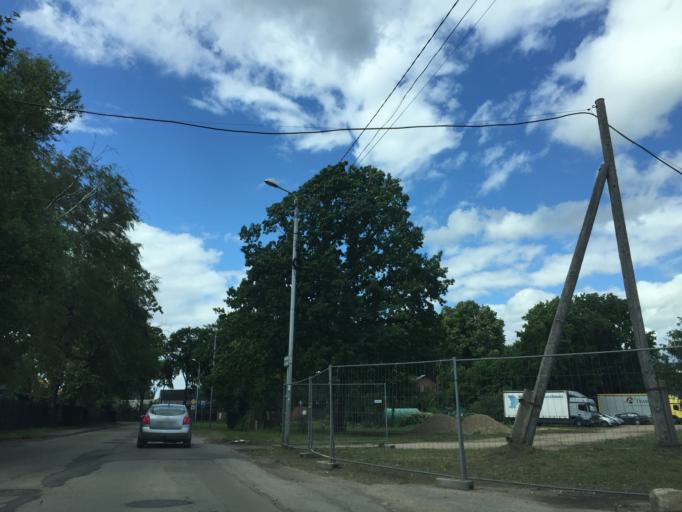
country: LV
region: Marupe
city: Marupe
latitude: 56.9448
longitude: 24.0378
